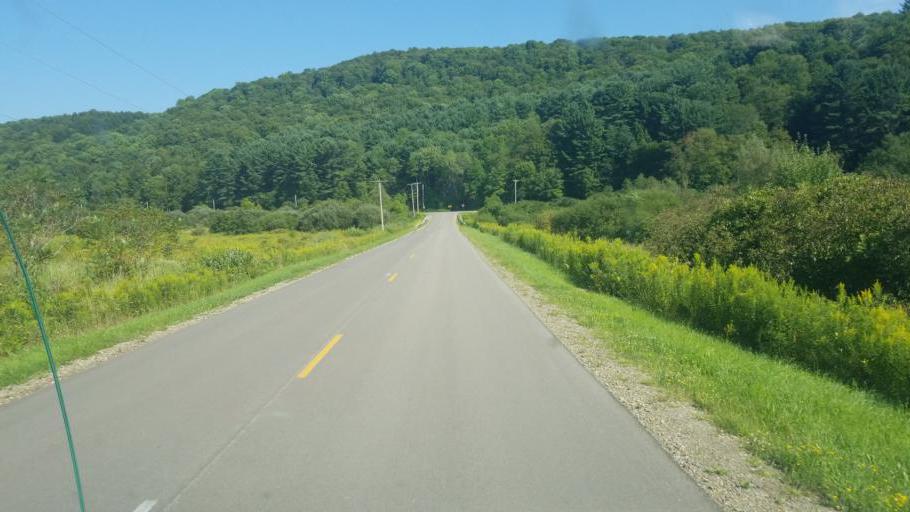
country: US
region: New York
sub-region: Allegany County
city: Wellsville
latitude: 42.0236
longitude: -77.9505
